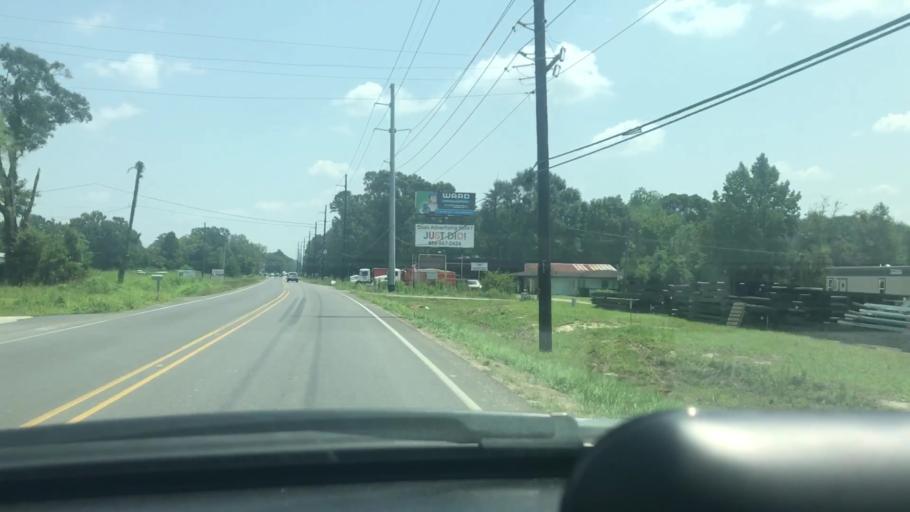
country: US
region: Louisiana
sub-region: Livingston Parish
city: Denham Springs
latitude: 30.4829
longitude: -90.9120
